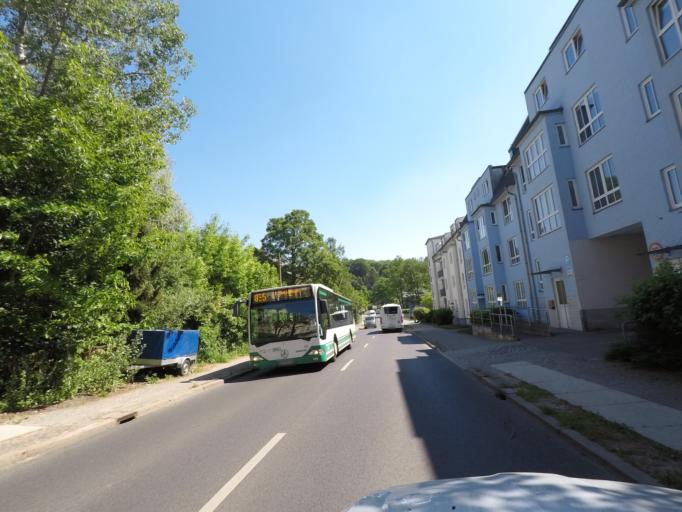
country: DE
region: Brandenburg
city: Eberswalde
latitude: 52.8294
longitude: 13.8069
